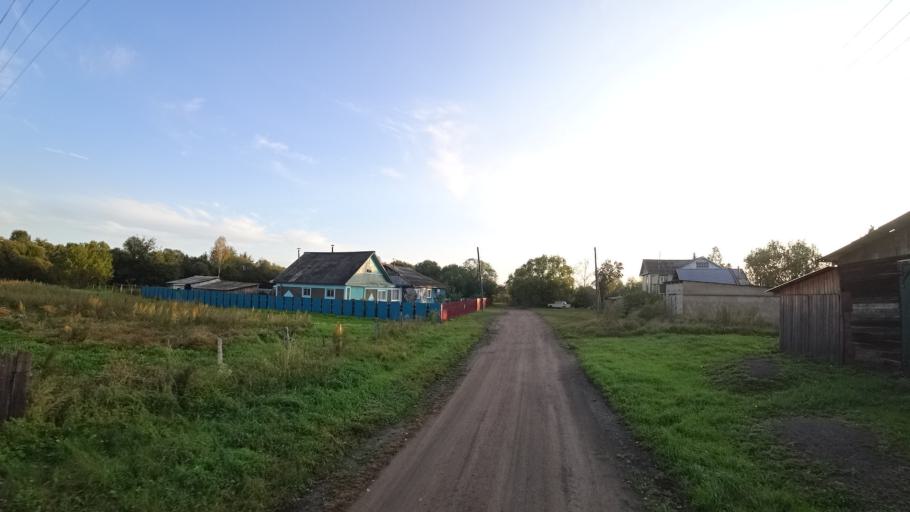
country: RU
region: Amur
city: Arkhara
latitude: 49.3644
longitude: 130.1137
